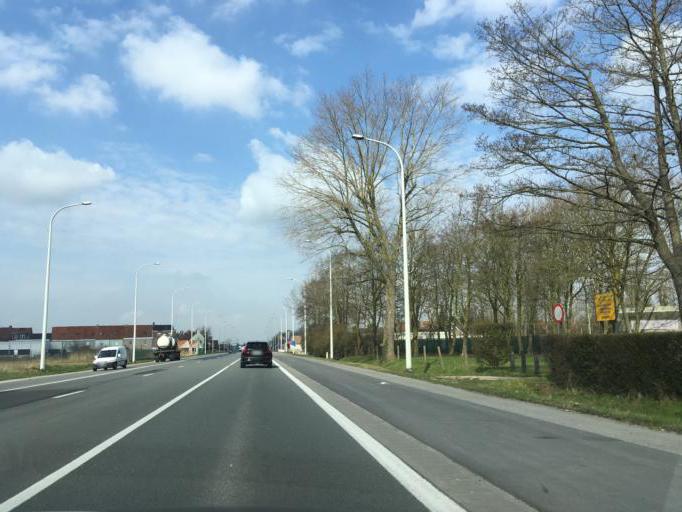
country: BE
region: Flanders
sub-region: Provincie West-Vlaanderen
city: Izegem
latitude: 50.9114
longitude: 3.2039
